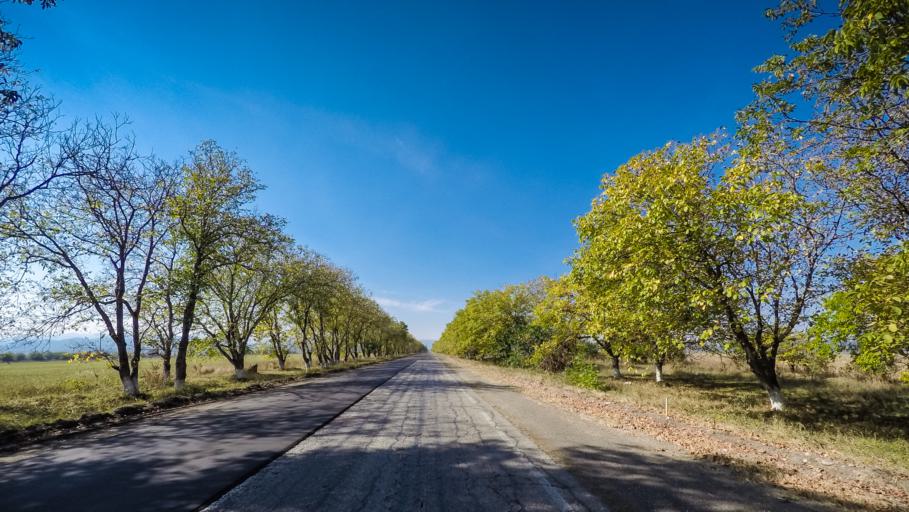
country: RU
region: Kabardino-Balkariya
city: Kamenka
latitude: 43.5694
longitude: 43.5090
